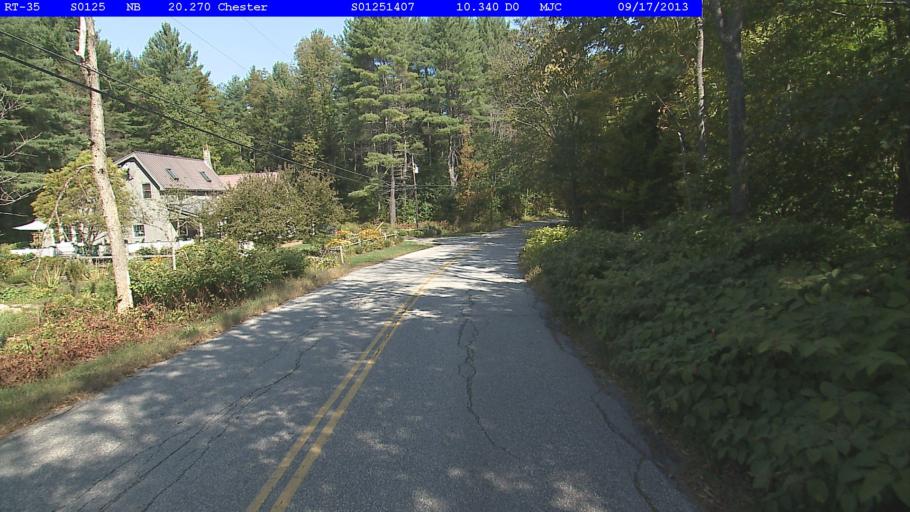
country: US
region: Vermont
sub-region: Windsor County
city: Chester
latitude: 43.2524
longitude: -72.6039
